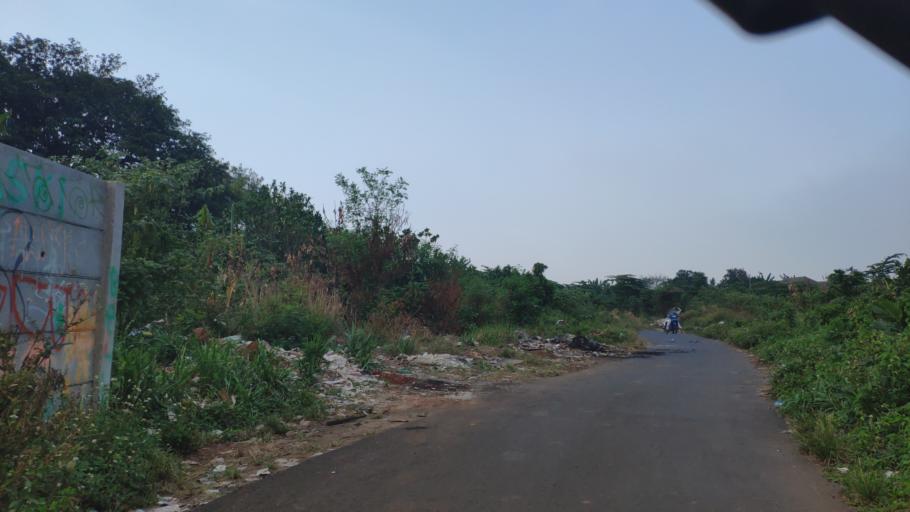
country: ID
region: Jakarta Raya
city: Jakarta
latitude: -6.2916
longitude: 106.8149
